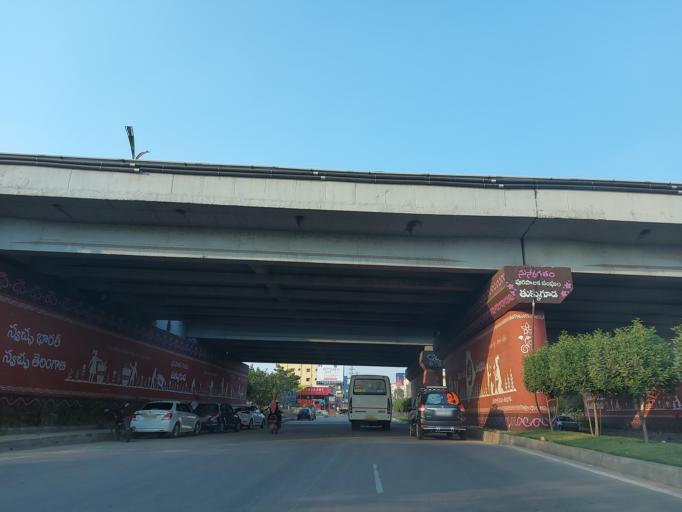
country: IN
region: Telangana
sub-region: Rangareddi
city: Balapur
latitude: 17.2035
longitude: 78.4761
